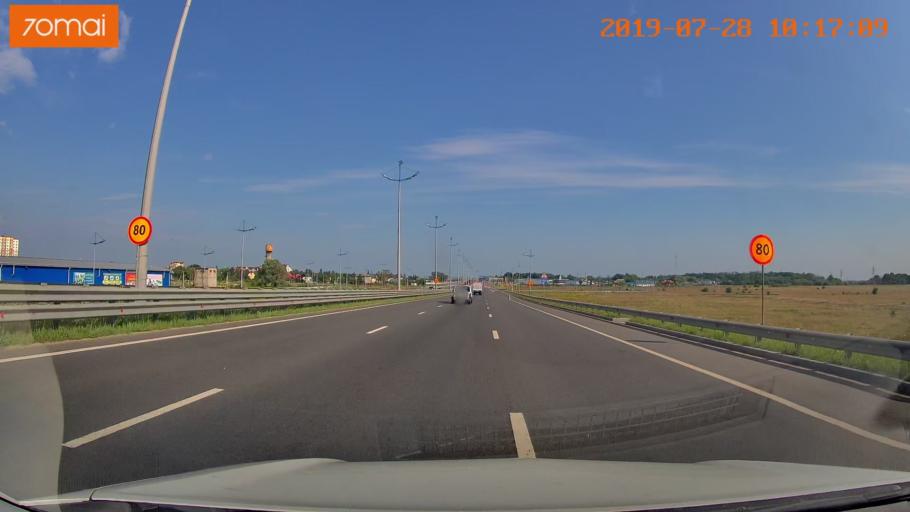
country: RU
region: Kaliningrad
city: Maloye Isakovo
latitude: 54.7363
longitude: 20.5960
